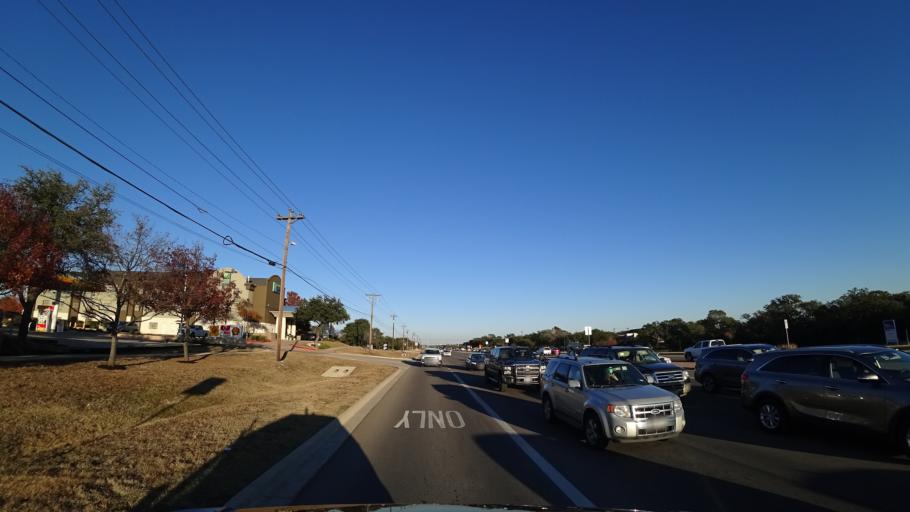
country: US
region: Texas
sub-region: Williamson County
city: Cedar Park
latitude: 30.5284
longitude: -97.8055
